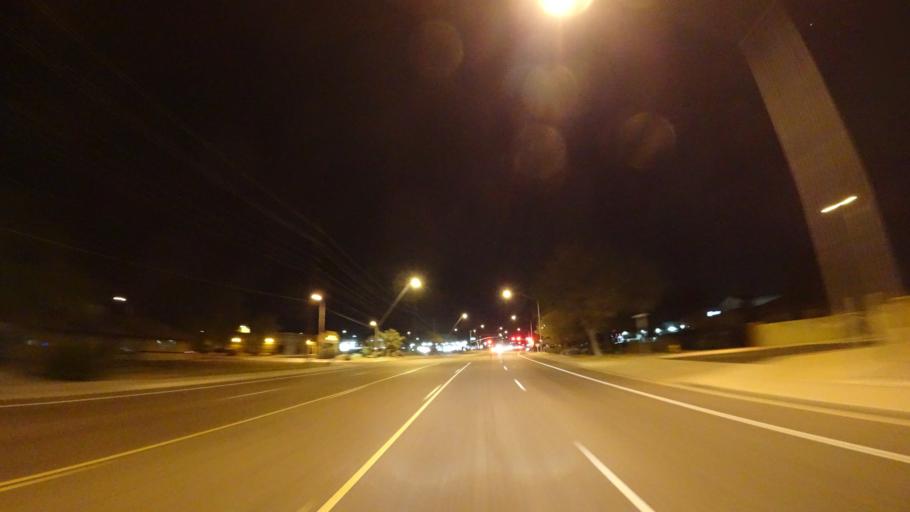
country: US
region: Arizona
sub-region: Maricopa County
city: Gilbert
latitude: 33.4374
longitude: -111.6866
